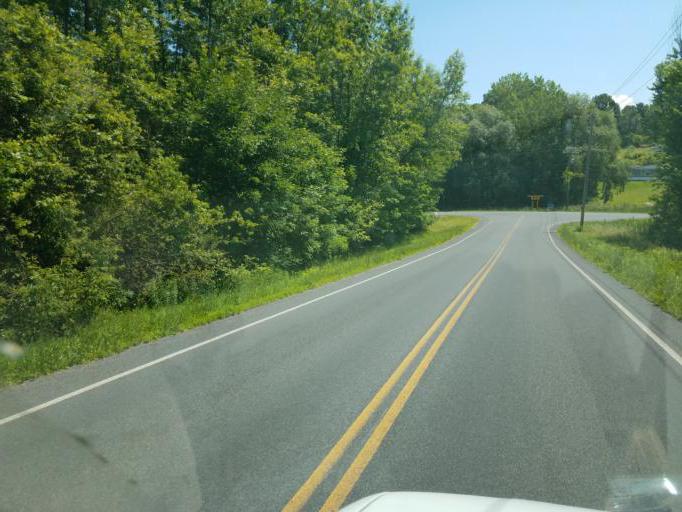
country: US
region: New York
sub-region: Wayne County
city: Wolcott
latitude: 43.2543
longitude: -76.9246
